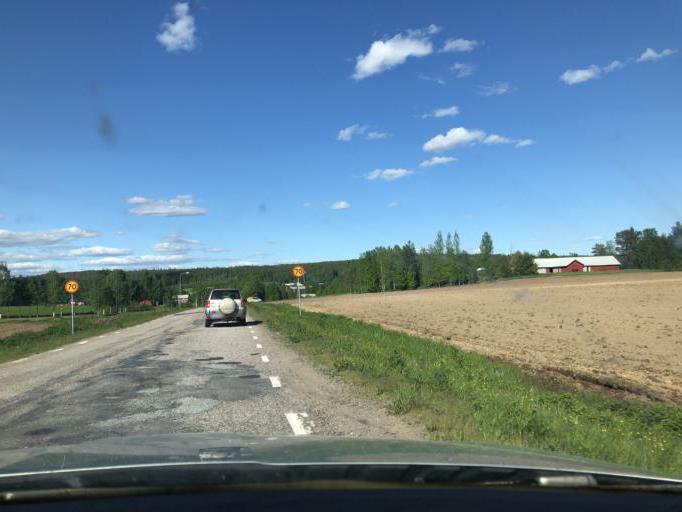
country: SE
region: Norrbotten
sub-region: Kalix Kommun
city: Kalix
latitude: 65.9861
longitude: 23.1437
